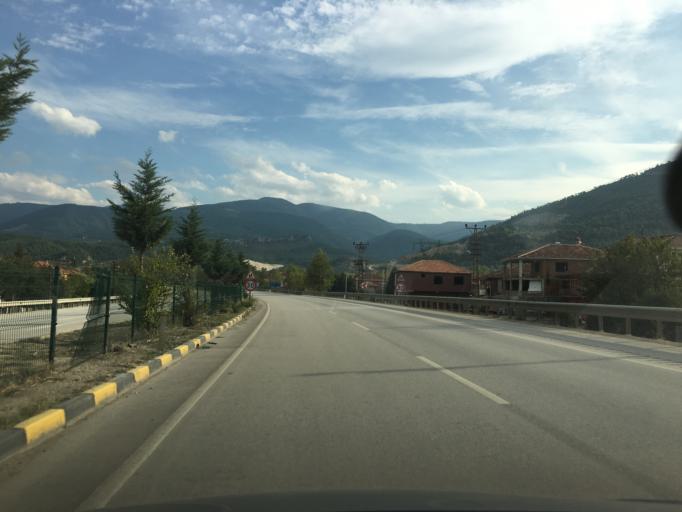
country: TR
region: Karabuk
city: Karabuk
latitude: 41.1028
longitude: 32.6693
